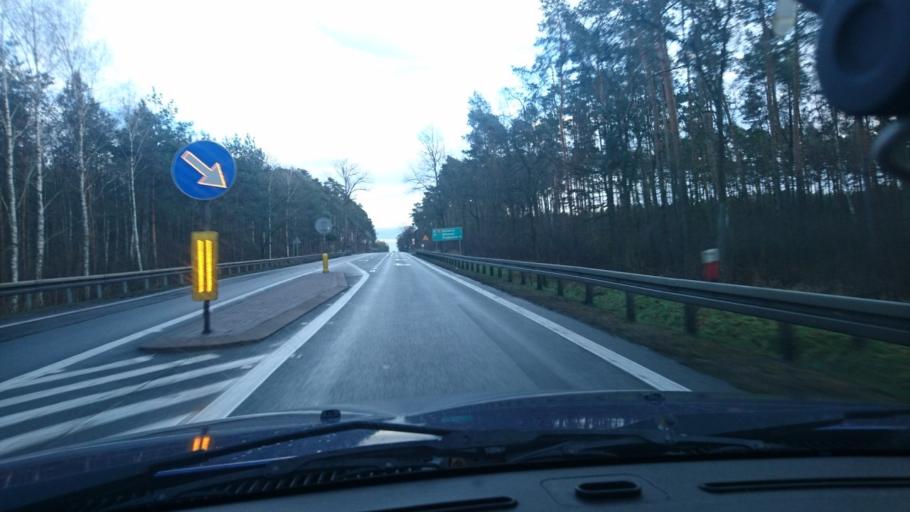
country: PL
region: Greater Poland Voivodeship
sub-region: Powiat kepinski
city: Kepno
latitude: 51.3268
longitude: 17.9632
